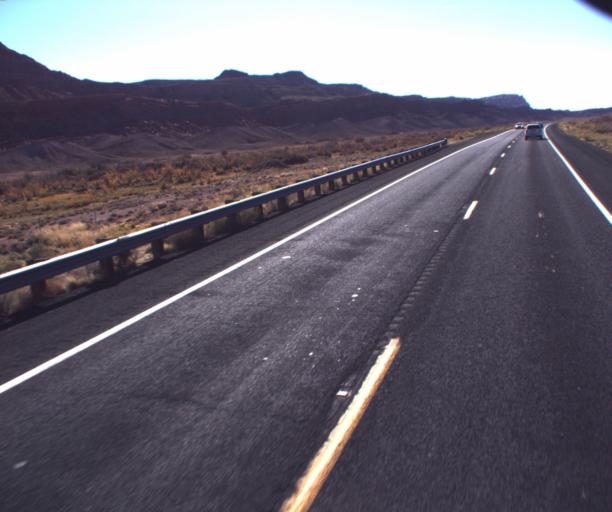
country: US
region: Arizona
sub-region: Coconino County
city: Tuba City
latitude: 36.2187
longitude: -111.3969
